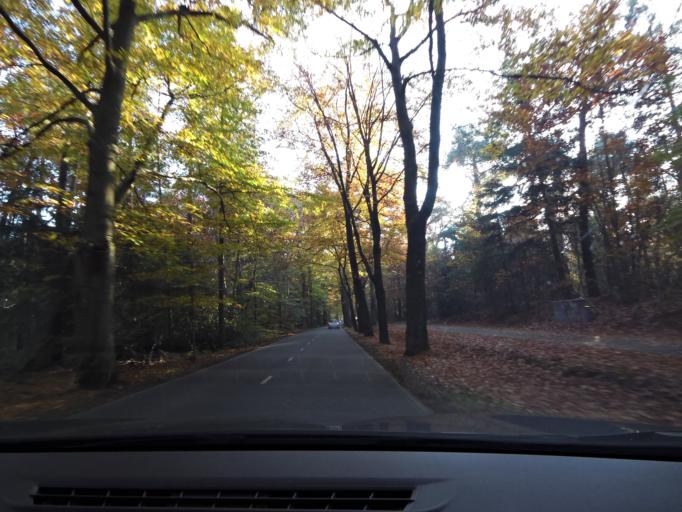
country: NL
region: North Brabant
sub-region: Gemeente Breda
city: Breda
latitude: 51.5345
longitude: 4.7727
